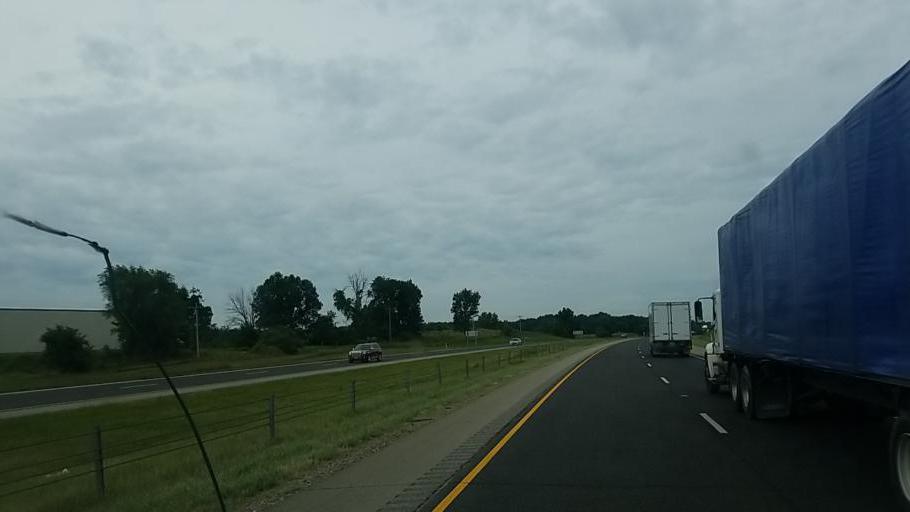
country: US
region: Indiana
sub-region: Steuben County
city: Angola
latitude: 41.6696
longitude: -85.0129
